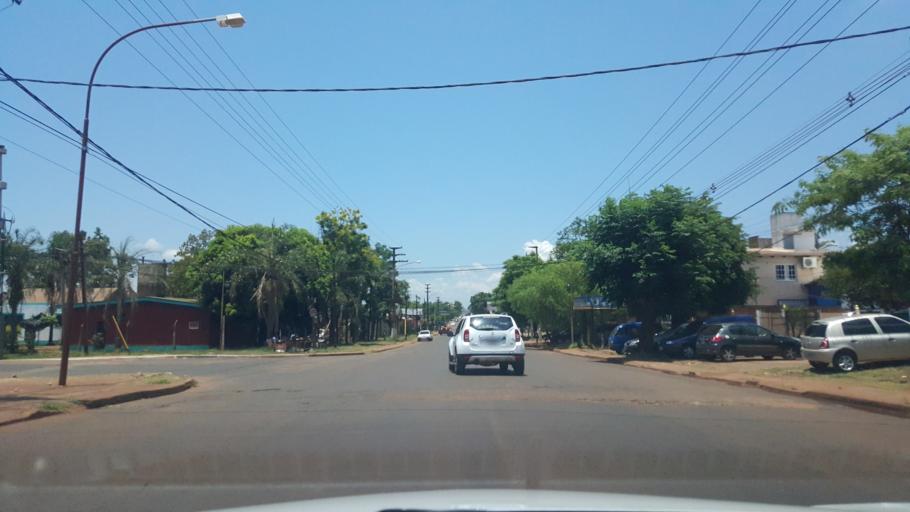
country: AR
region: Misiones
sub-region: Departamento de Capital
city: Posadas
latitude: -27.4051
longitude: -55.9112
